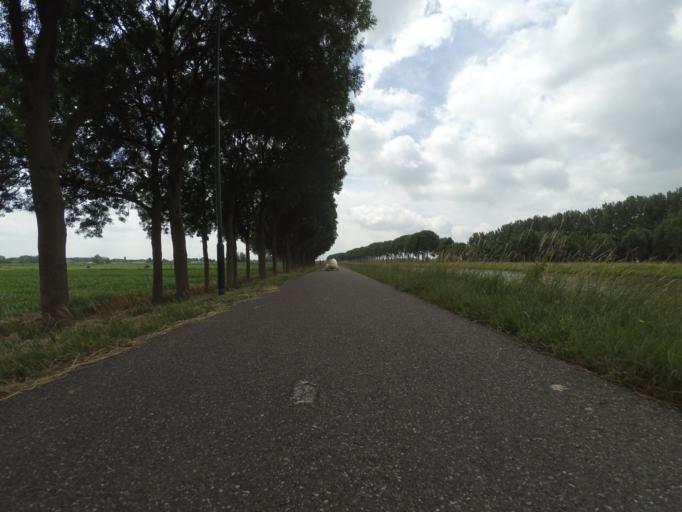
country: NL
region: South Holland
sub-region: Gemeente Gorinchem
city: Gorinchem
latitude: 51.8596
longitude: 4.9849
